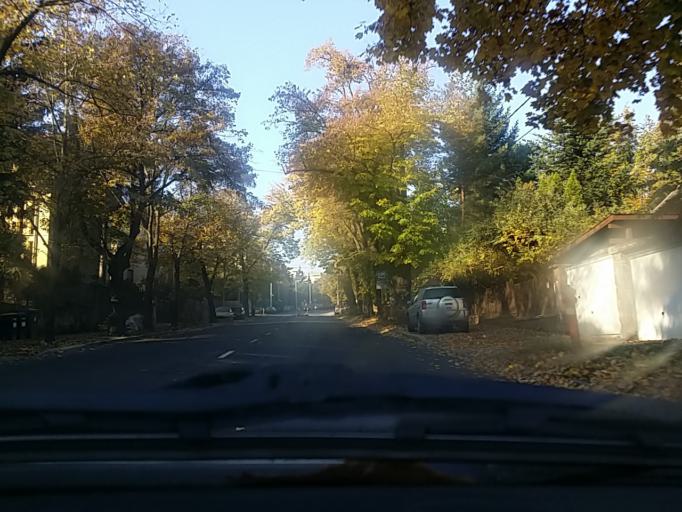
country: HU
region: Budapest
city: Budapest II. keruelet
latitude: 47.5298
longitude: 19.0199
